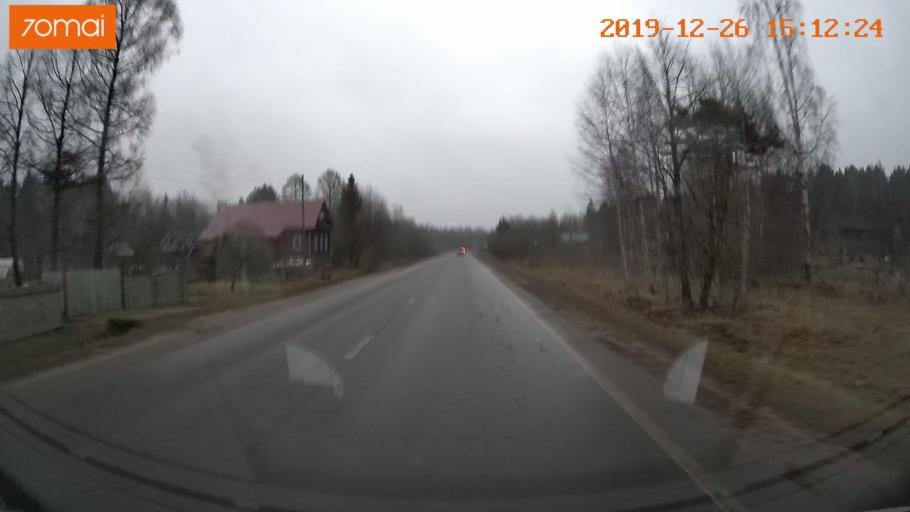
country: RU
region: Jaroslavl
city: Rybinsk
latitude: 58.1278
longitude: 38.8750
